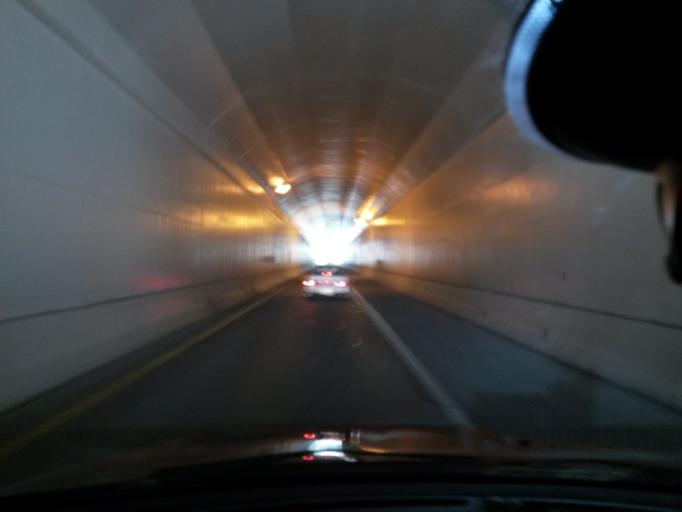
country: US
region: Virginia
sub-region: Roanoke County
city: Hollins
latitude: 37.3323
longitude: -79.9670
